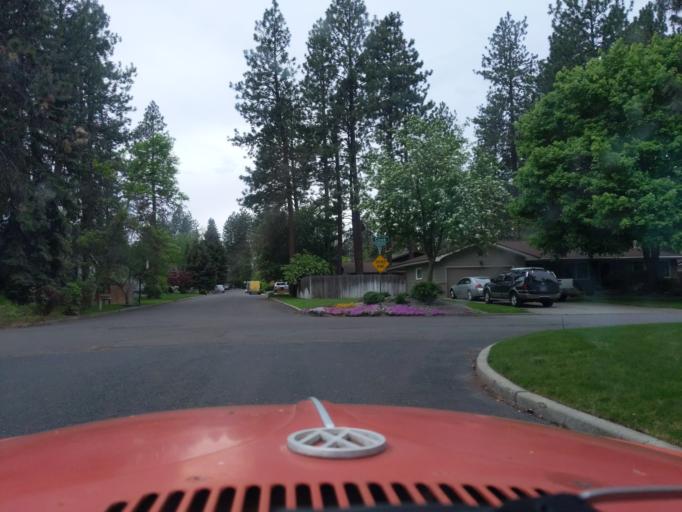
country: US
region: Washington
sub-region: Spokane County
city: Spokane
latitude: 47.6182
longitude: -117.3737
